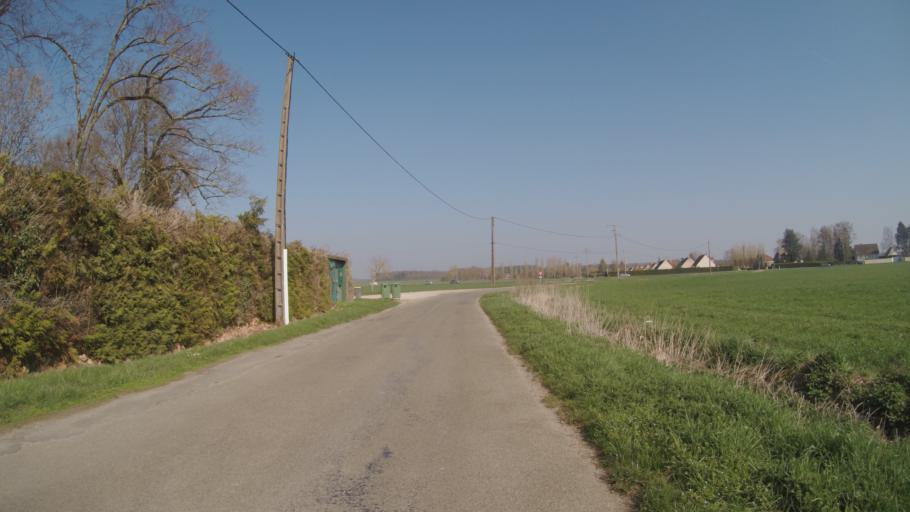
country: FR
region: Centre
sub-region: Departement du Loiret
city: Boigny-sur-Bionne
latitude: 47.9264
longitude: 2.0438
